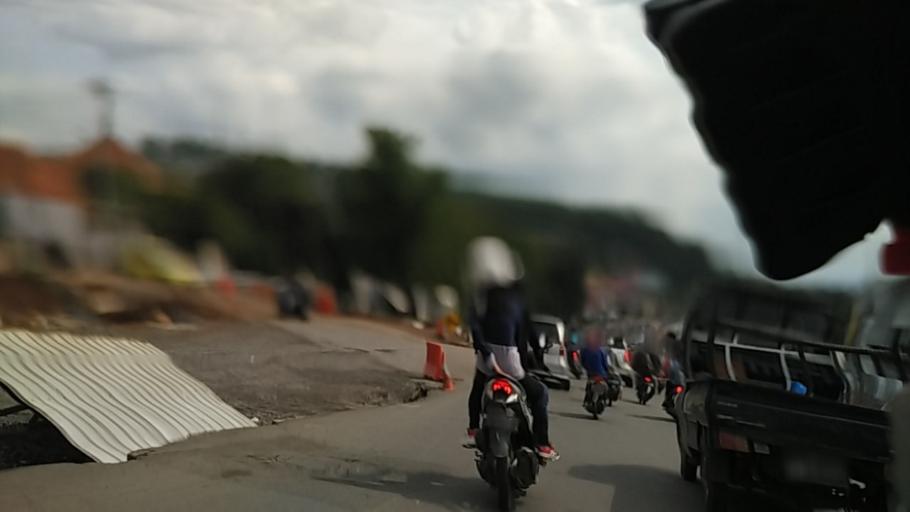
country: ID
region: Central Java
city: Semarang
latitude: -7.0288
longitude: 110.4184
